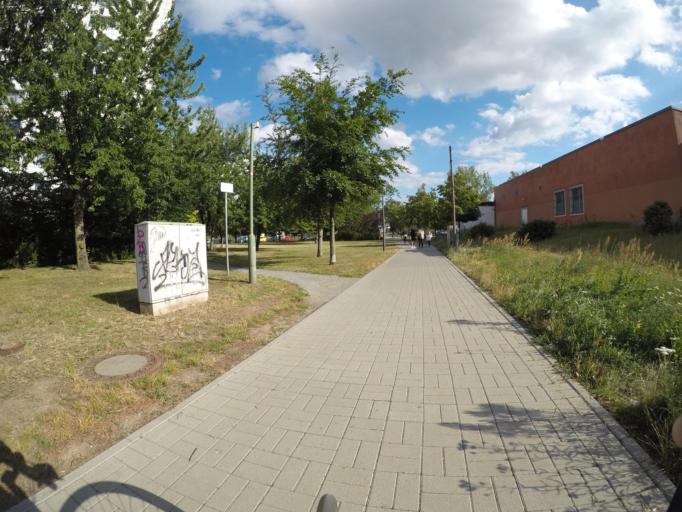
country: DE
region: Berlin
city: Marzahn
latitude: 52.5443
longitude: 13.5493
